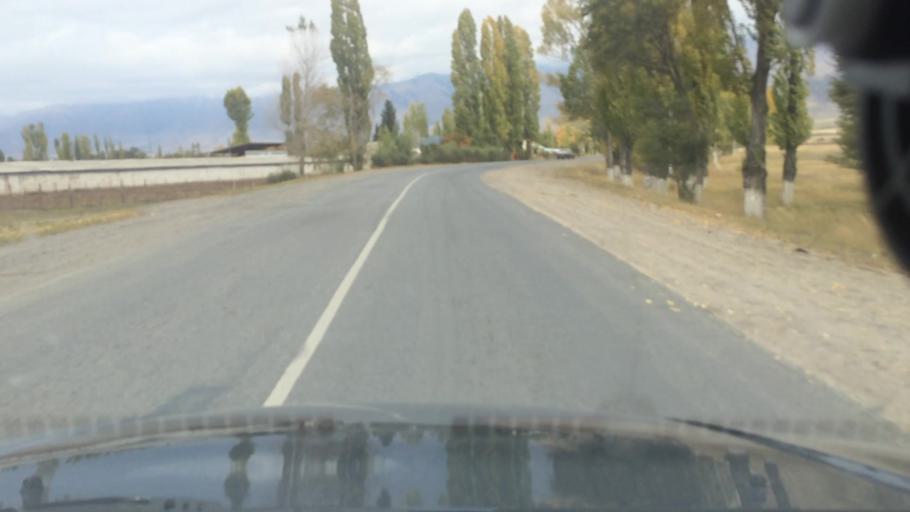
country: KG
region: Ysyk-Koel
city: Tyup
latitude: 42.7424
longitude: 78.3403
